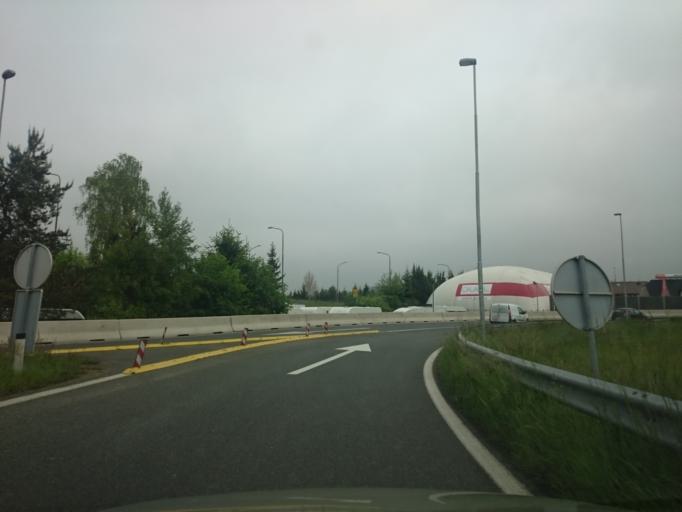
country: SI
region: Celje
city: Trnovlje pri Celju
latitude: 46.2551
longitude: 15.2834
